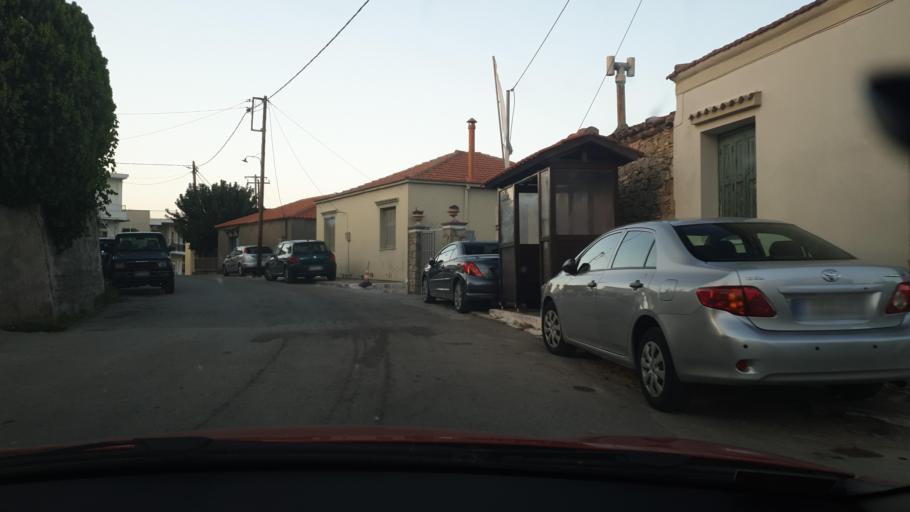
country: GR
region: Central Greece
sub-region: Nomos Evvoias
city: Oxilithos
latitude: 38.5846
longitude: 24.1117
